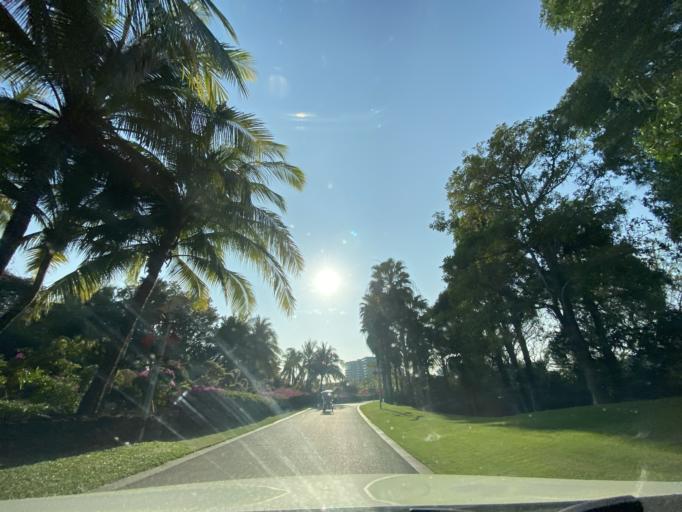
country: CN
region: Hainan
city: Xincun
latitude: 18.4175
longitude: 109.9553
